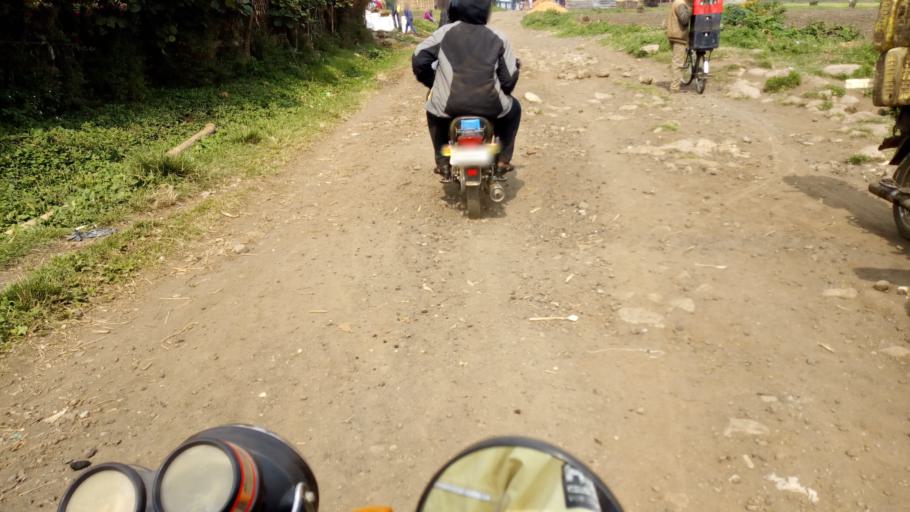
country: UG
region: Western Region
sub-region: Kisoro District
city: Kisoro
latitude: -1.3323
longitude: 29.6093
